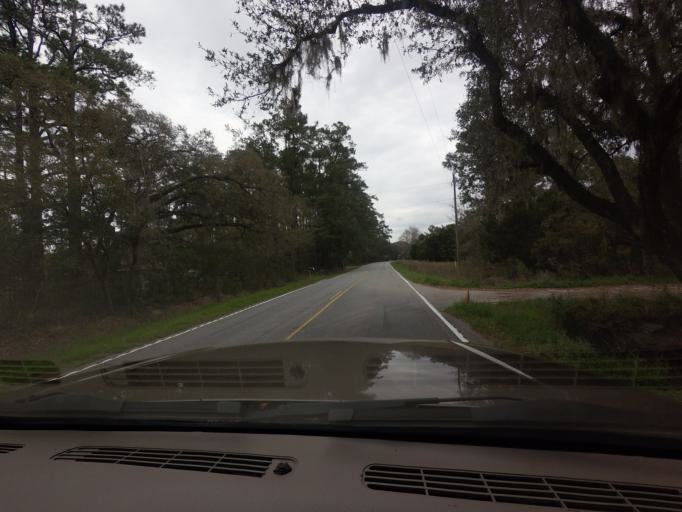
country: US
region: South Carolina
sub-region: Charleston County
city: Meggett
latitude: 32.7101
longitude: -80.2896
